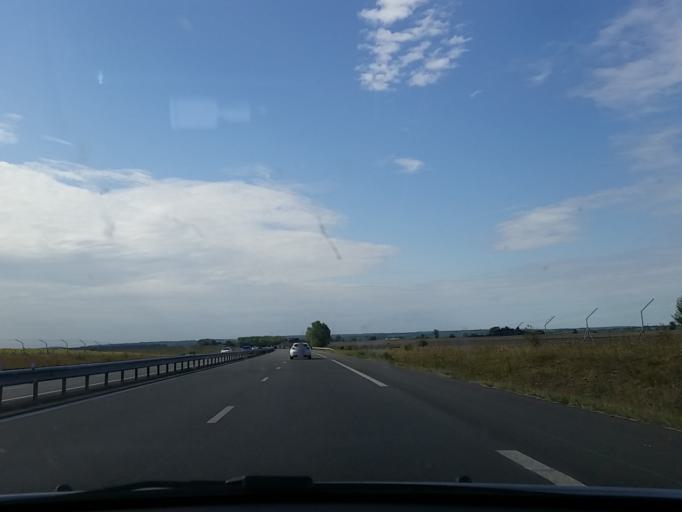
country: FR
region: Centre
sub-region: Departement du Cher
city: Levet
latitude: 46.8361
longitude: 2.4136
